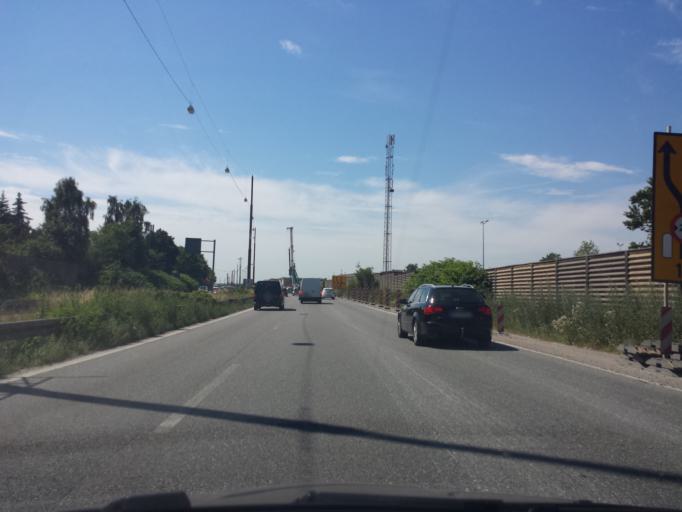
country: DK
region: Capital Region
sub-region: Hvidovre Kommune
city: Hvidovre
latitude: 55.6528
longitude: 12.4851
